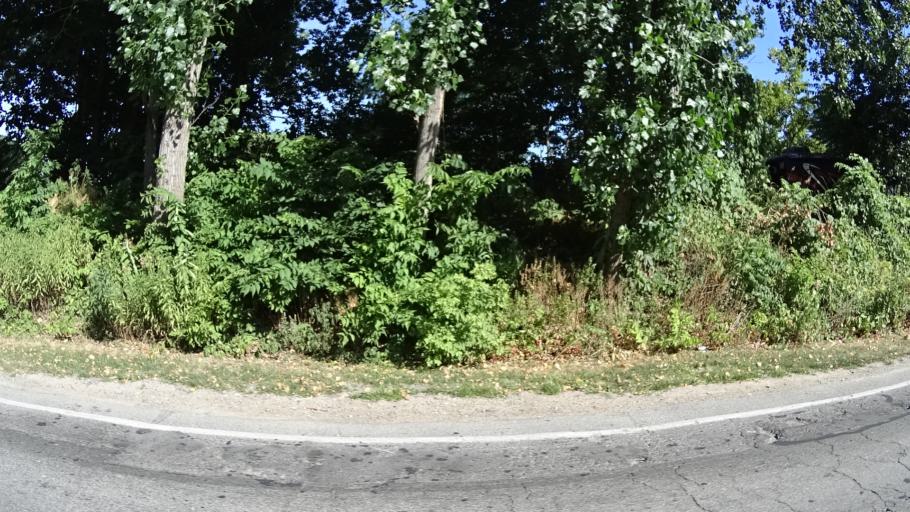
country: US
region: Ohio
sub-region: Erie County
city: Sandusky
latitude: 41.4871
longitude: -82.6931
